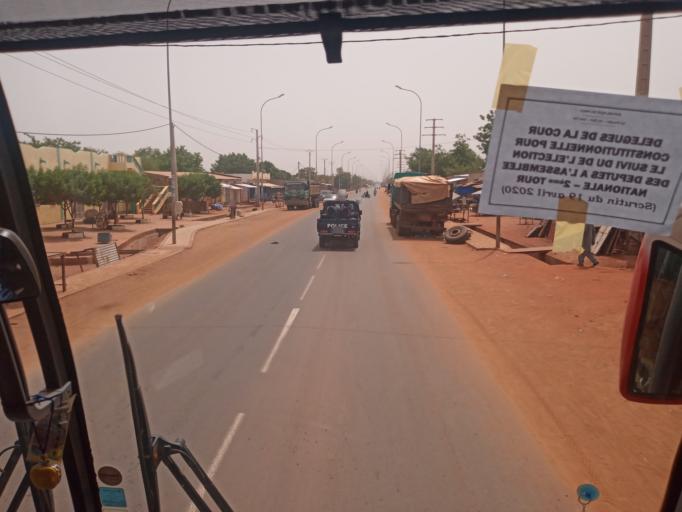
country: ML
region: Koulikoro
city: Koulikoro
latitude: 12.8448
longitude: -7.5821
